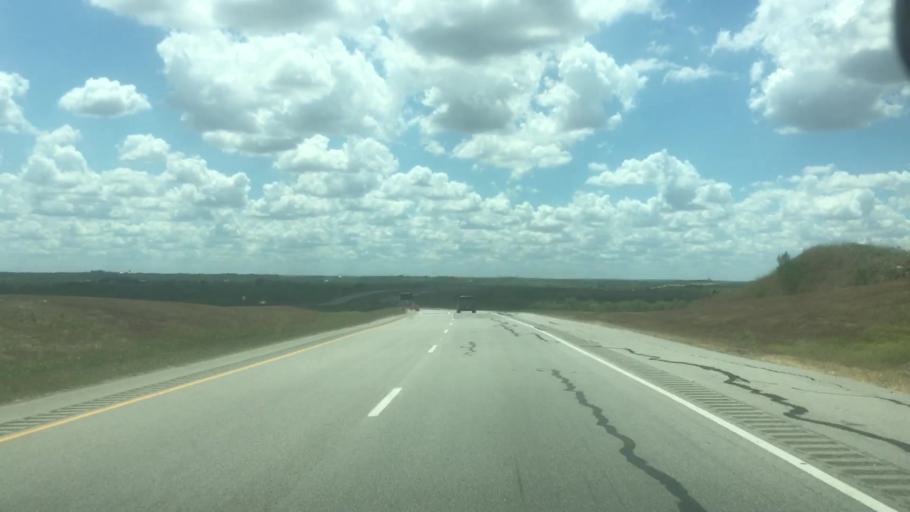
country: US
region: Texas
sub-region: Caldwell County
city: Lockhart
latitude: 29.8476
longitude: -97.7262
